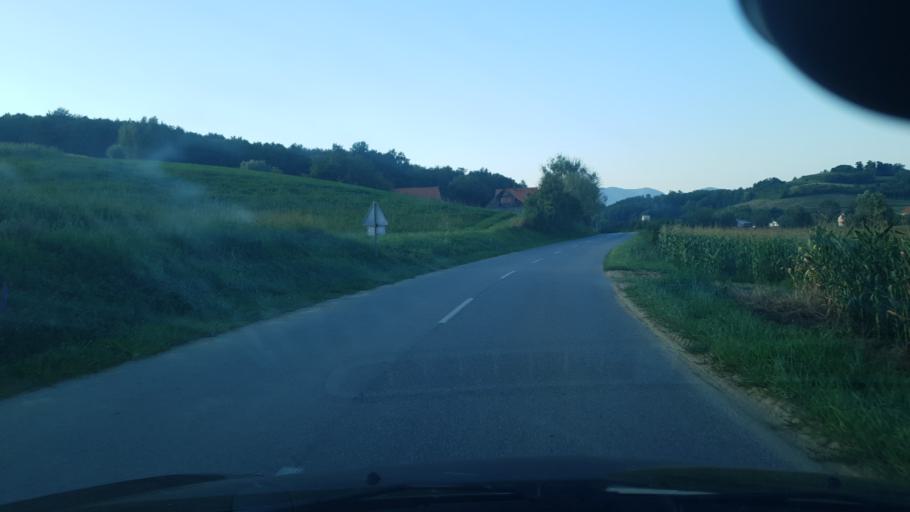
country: HR
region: Krapinsko-Zagorska
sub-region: Grad Krapina
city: Krapina
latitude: 46.1094
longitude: 15.8723
